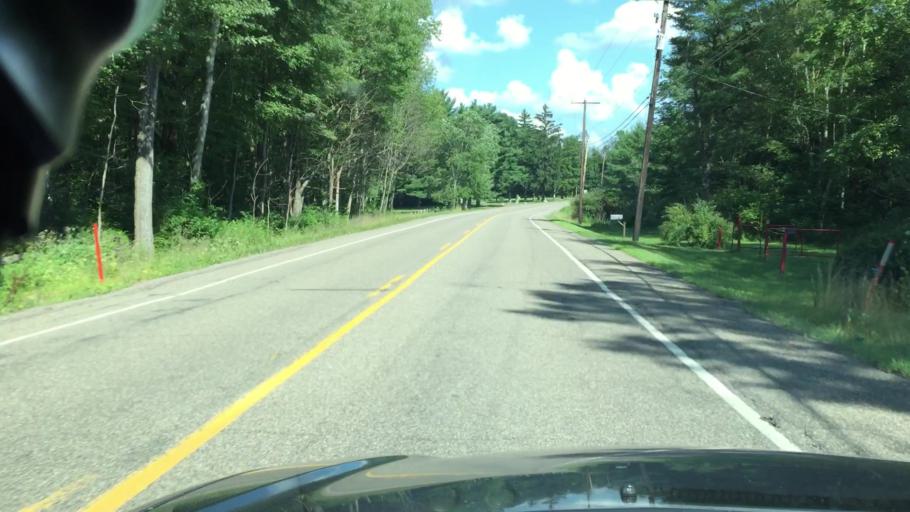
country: US
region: Pennsylvania
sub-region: Carbon County
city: Weatherly
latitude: 40.9262
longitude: -75.8695
